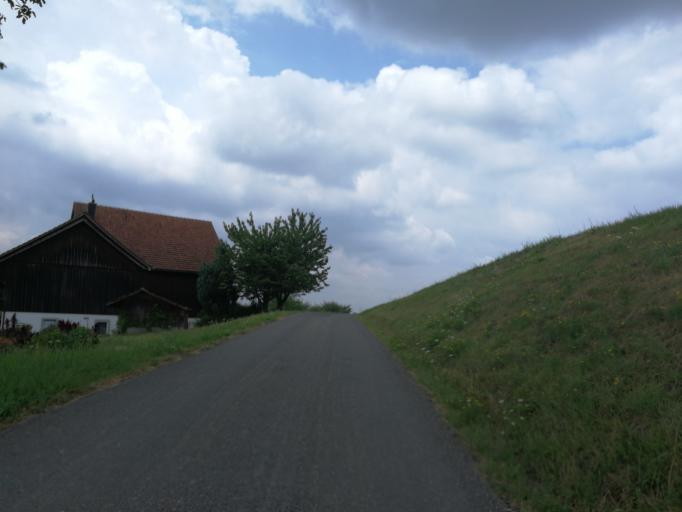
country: CH
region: Zurich
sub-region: Bezirk Hinwil
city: Gruet
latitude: 47.2960
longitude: 8.7740
